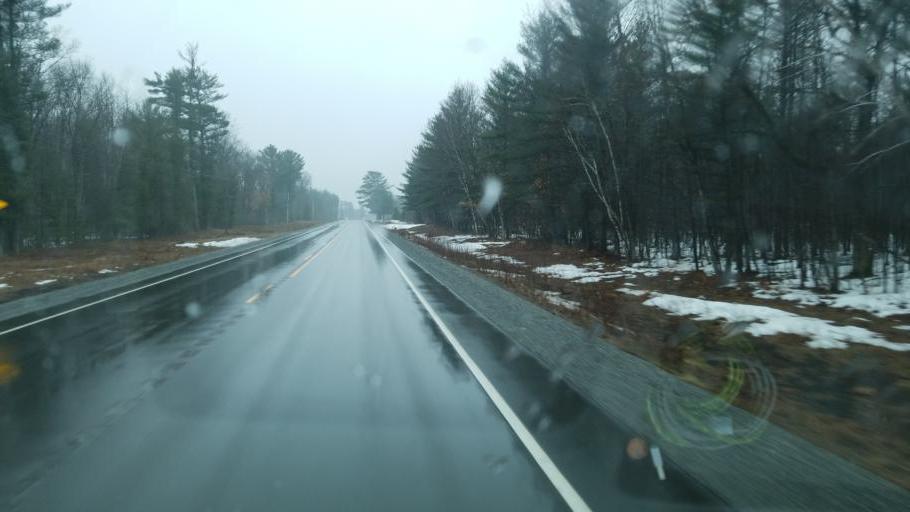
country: US
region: Wisconsin
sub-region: Clark County
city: Neillsville
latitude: 44.4800
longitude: -90.3556
